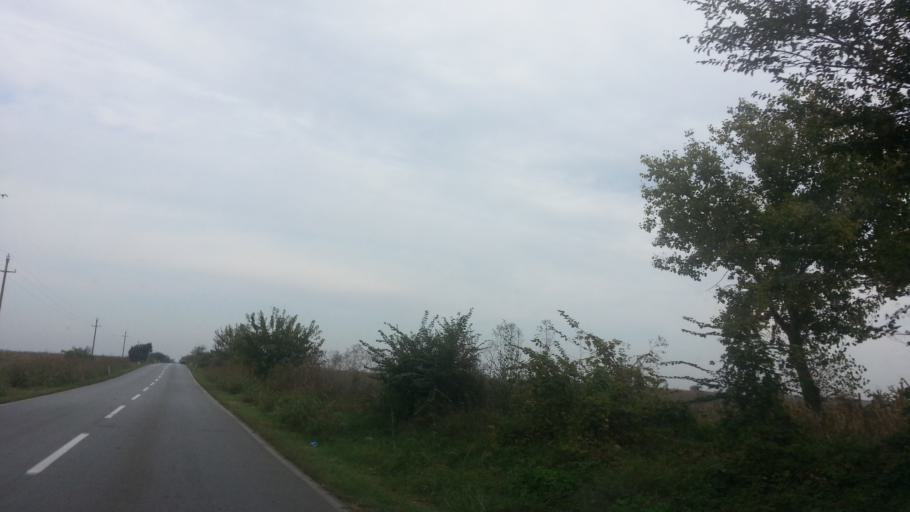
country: RS
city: Belegis
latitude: 45.0477
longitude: 20.3323
